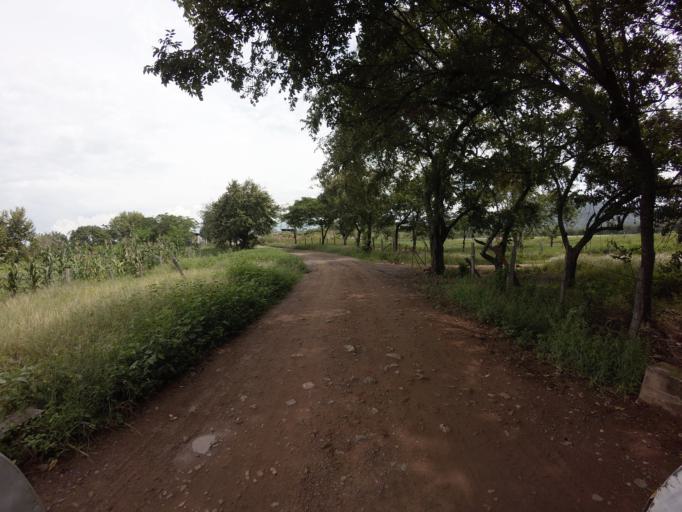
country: CO
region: Tolima
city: Natagaima
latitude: 3.4452
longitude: -75.1393
